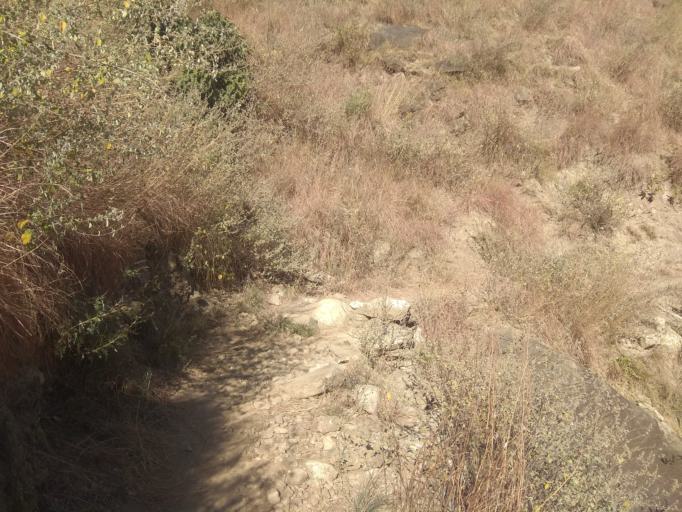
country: NP
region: Mid Western
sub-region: Bheri Zone
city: Dailekh
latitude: 29.2573
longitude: 81.6755
